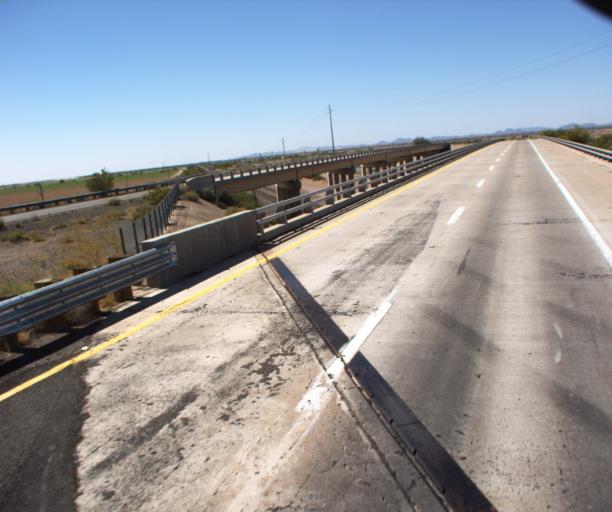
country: US
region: Arizona
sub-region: Maricopa County
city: Gila Bend
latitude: 32.9418
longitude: -112.7394
